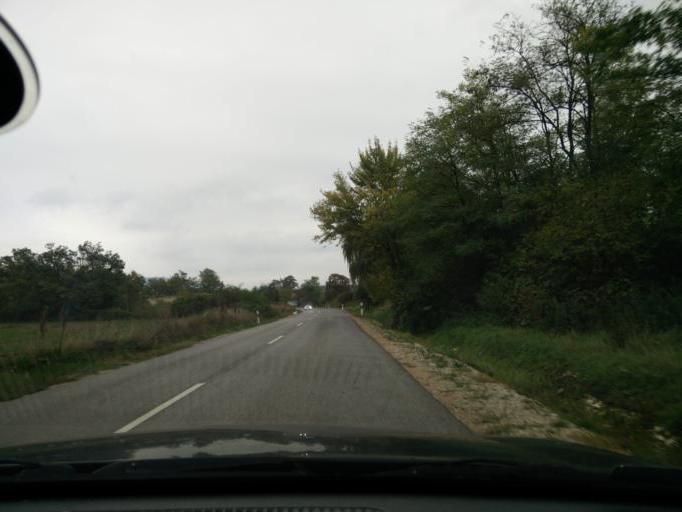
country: HU
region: Komarom-Esztergom
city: Tokod
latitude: 47.7016
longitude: 18.6221
